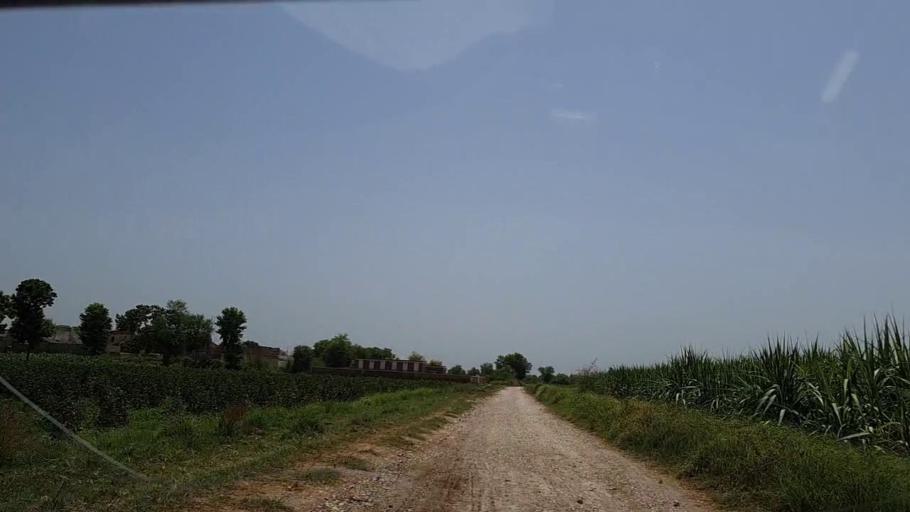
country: PK
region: Sindh
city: Tharu Shah
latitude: 26.9291
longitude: 68.0408
